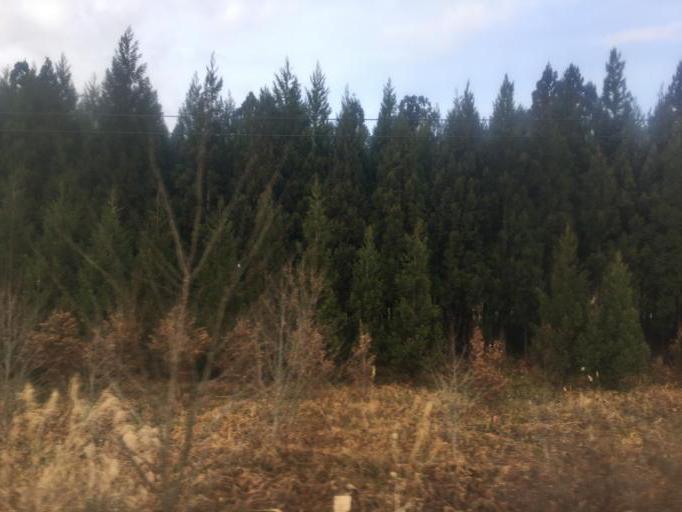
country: JP
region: Akita
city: Takanosu
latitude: 40.2455
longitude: 140.3914
